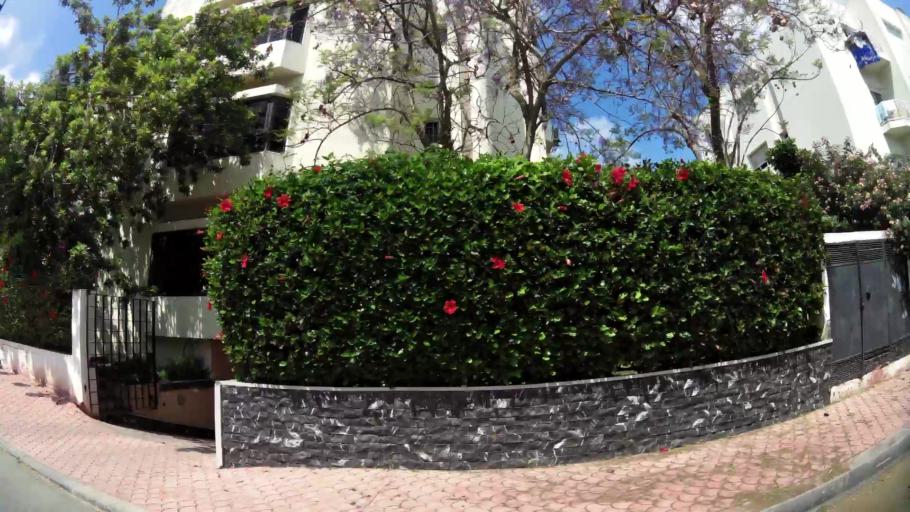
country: MA
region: Rabat-Sale-Zemmour-Zaer
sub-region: Skhirate-Temara
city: Temara
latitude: 33.9560
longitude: -6.8823
